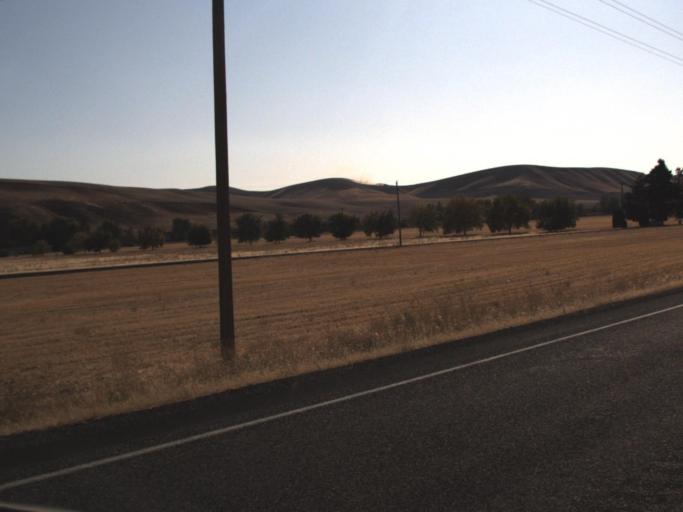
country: US
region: Washington
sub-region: Walla Walla County
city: Garrett
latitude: 46.2968
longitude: -118.4414
